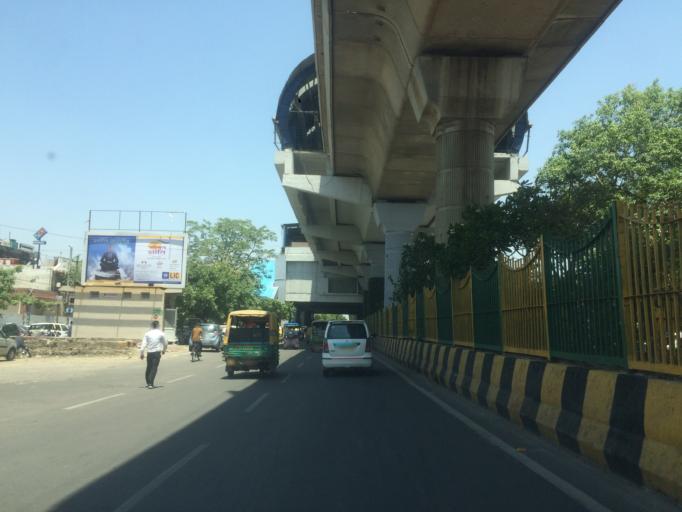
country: IN
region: Uttar Pradesh
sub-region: Gautam Buddha Nagar
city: Noida
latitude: 28.5775
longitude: 77.3185
